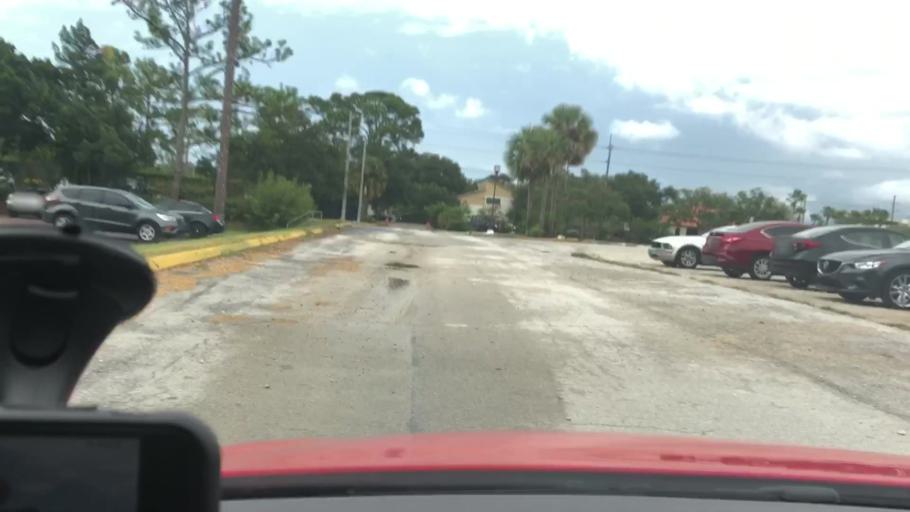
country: US
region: Florida
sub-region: Volusia County
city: Daytona Beach
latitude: 29.2049
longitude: -81.0593
